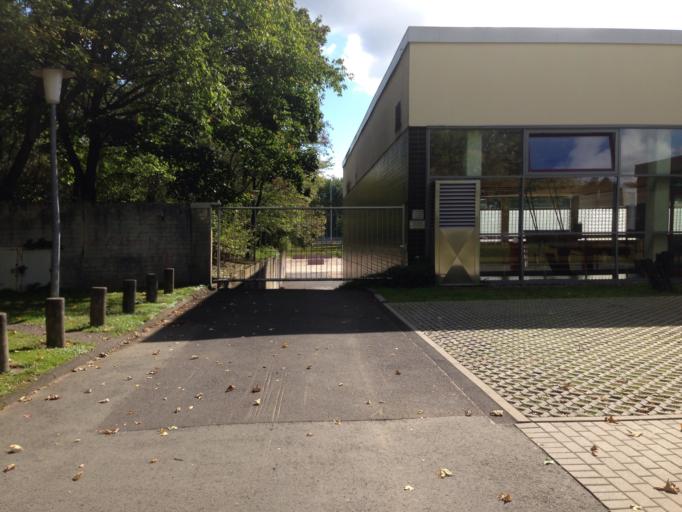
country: DE
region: Hesse
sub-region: Regierungsbezirk Giessen
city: Giessen
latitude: 50.5854
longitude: 8.7025
